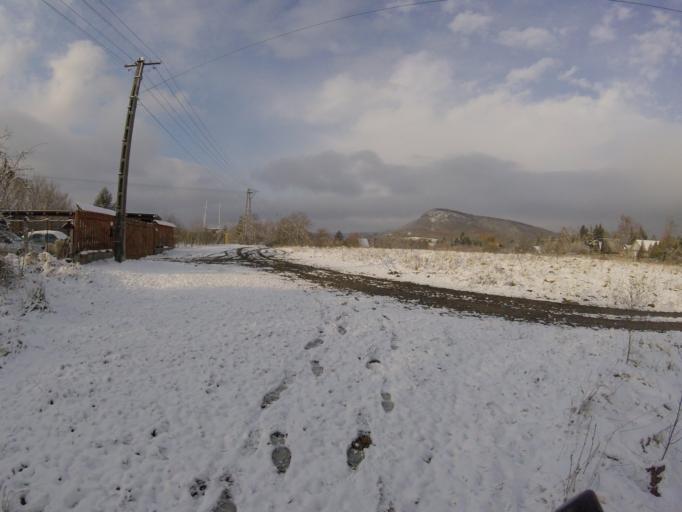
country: HU
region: Komarom-Esztergom
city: Esztergom
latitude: 47.7955
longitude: 18.8019
